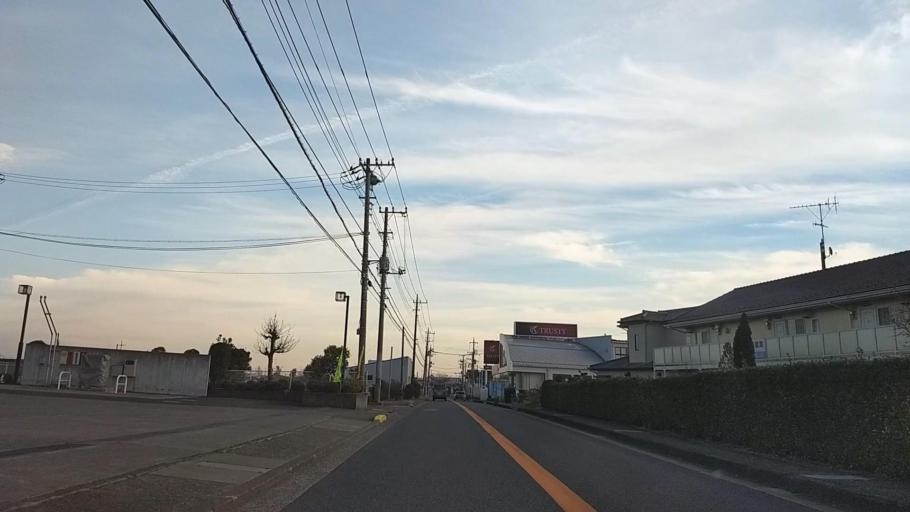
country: JP
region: Kanagawa
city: Atsugi
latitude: 35.4831
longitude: 139.3334
